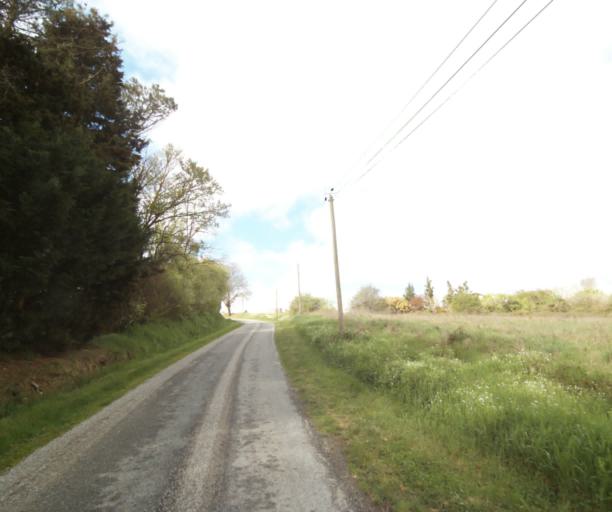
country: FR
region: Midi-Pyrenees
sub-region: Departement de l'Ariege
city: Saverdun
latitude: 43.2190
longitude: 1.5709
